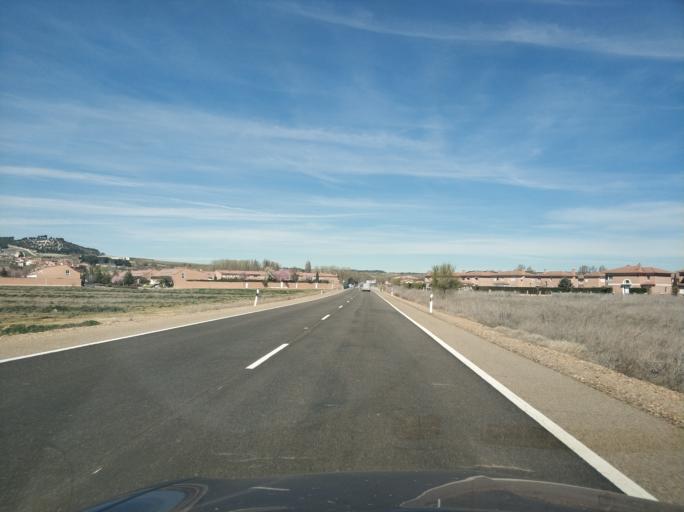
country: ES
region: Castille and Leon
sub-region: Provincia de Valladolid
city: Simancas
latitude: 41.5843
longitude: -4.8166
